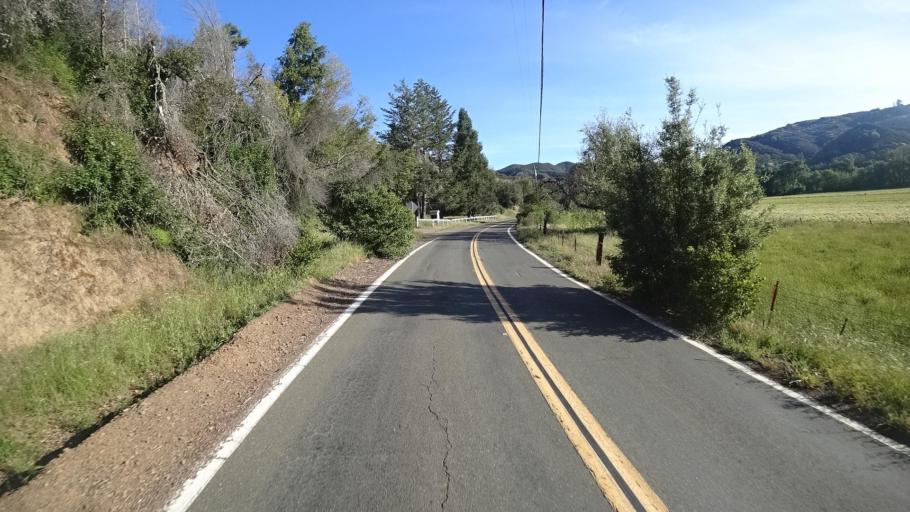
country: US
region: California
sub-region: Lake County
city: North Lakeport
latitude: 39.1178
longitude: -122.9887
